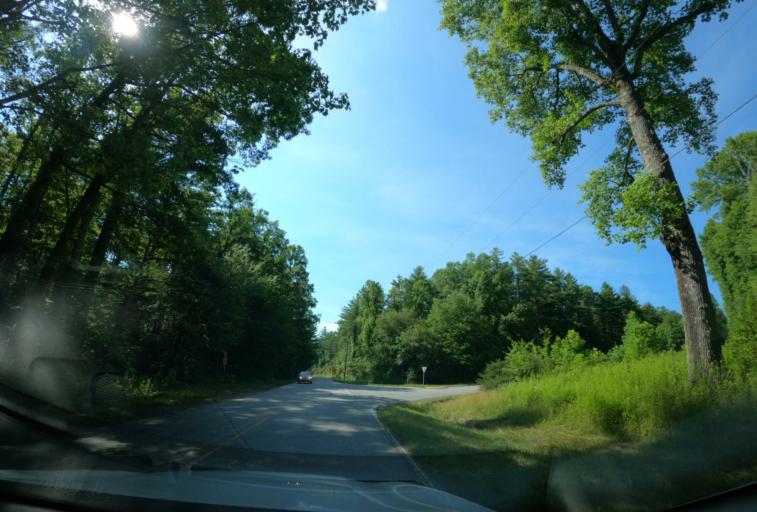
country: US
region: North Carolina
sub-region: Transylvania County
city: Brevard
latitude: 35.1818
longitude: -82.6416
